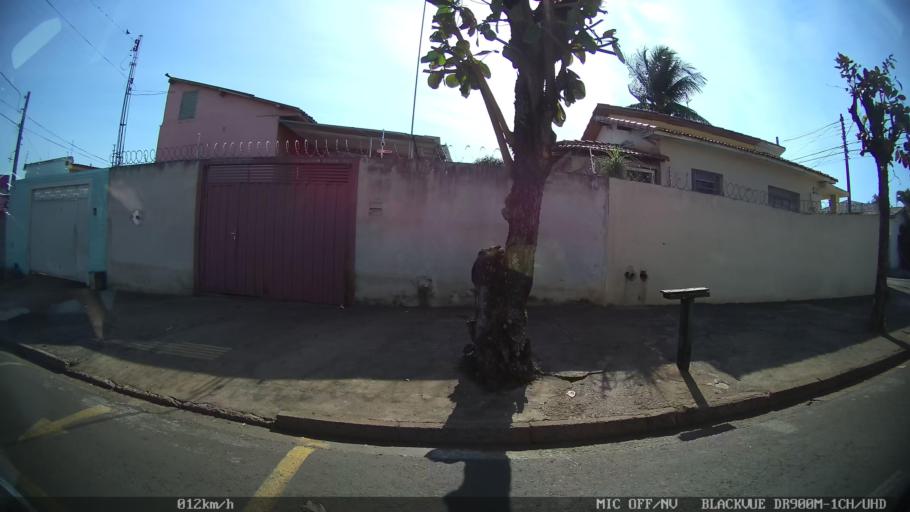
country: BR
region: Sao Paulo
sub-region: Sao Jose Do Rio Preto
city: Sao Jose do Rio Preto
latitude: -20.7906
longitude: -49.4037
